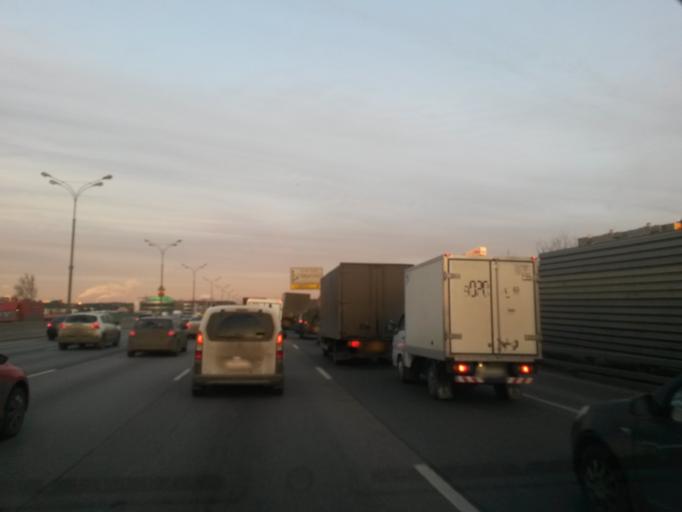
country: RU
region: Moskovskaya
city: Mosrentgen
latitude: 55.6257
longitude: 37.4753
